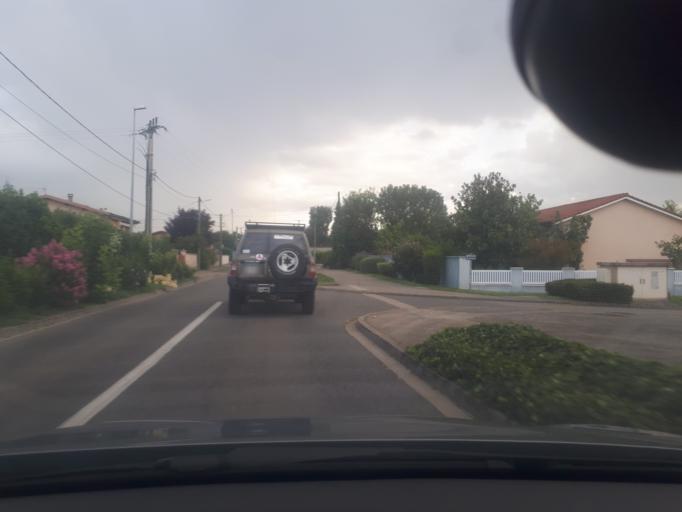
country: FR
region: Rhone-Alpes
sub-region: Departement du Rhone
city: Saint-Bonnet-de-Mure
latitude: 45.7014
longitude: 5.0299
